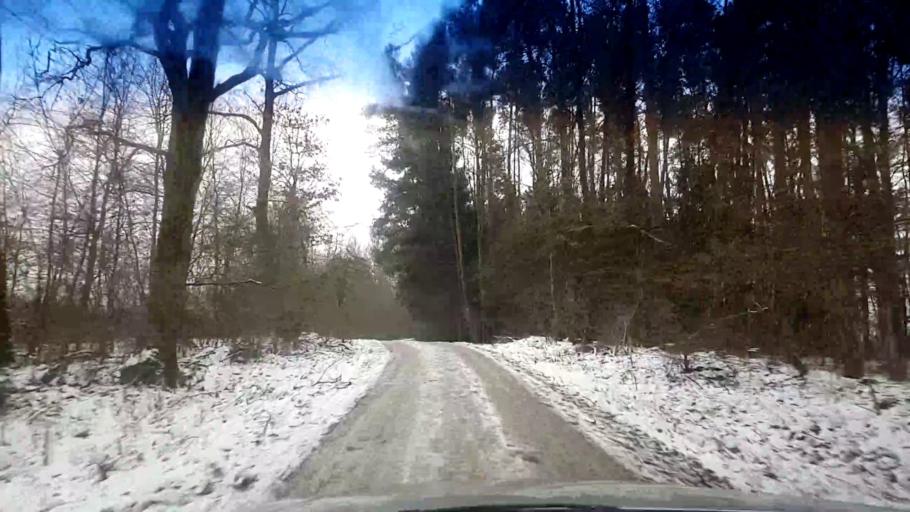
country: DE
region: Bavaria
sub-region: Upper Franconia
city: Gundelsheim
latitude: 49.9455
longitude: 10.9153
